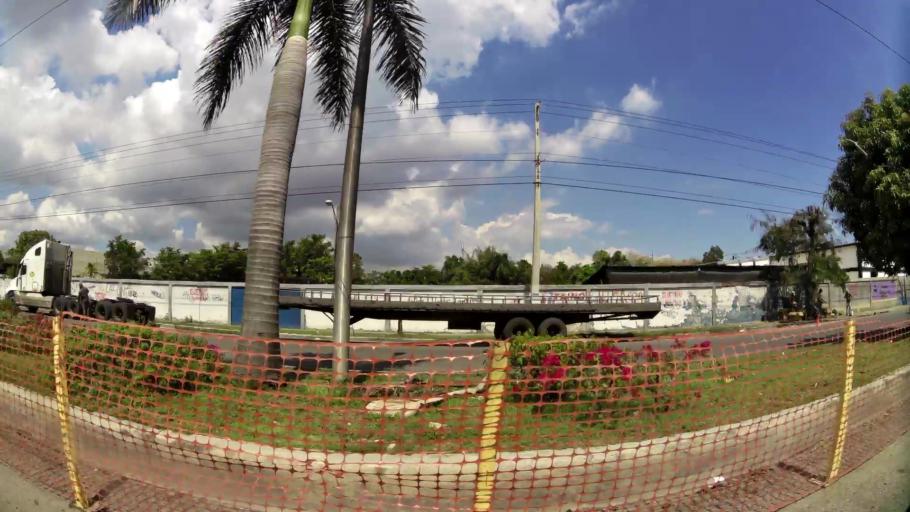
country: DO
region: Santo Domingo
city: Santo Domingo Oeste
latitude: 18.4854
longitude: -69.9991
